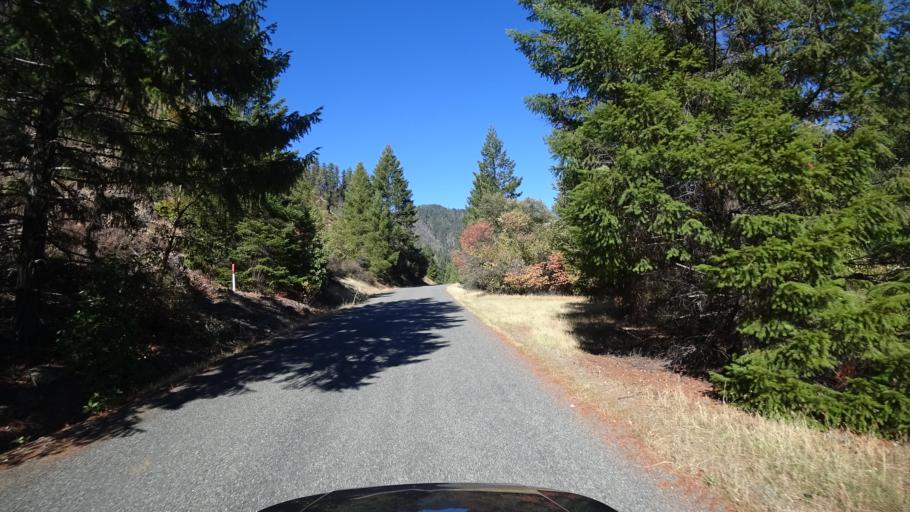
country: US
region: California
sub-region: Humboldt County
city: Willow Creek
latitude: 41.3083
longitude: -123.3747
